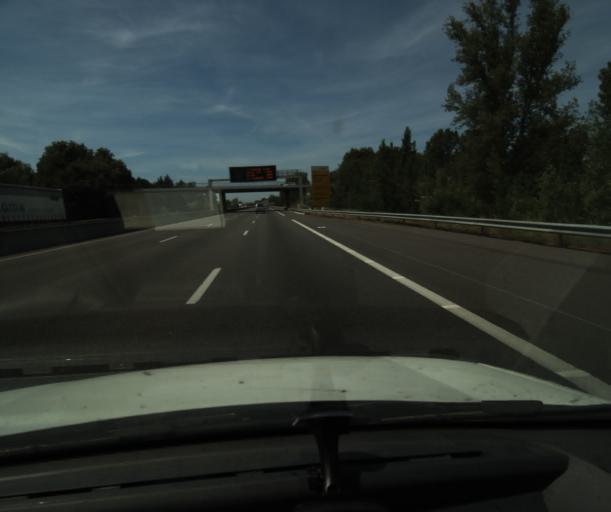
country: FR
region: Midi-Pyrenees
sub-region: Departement de la Haute-Garonne
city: Labege
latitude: 43.5266
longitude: 1.5180
